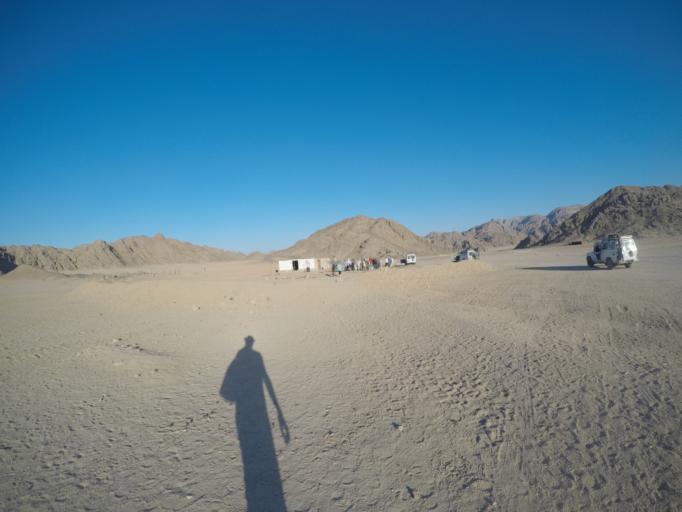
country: EG
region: Red Sea
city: El Gouna
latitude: 27.1512
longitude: 33.5442
